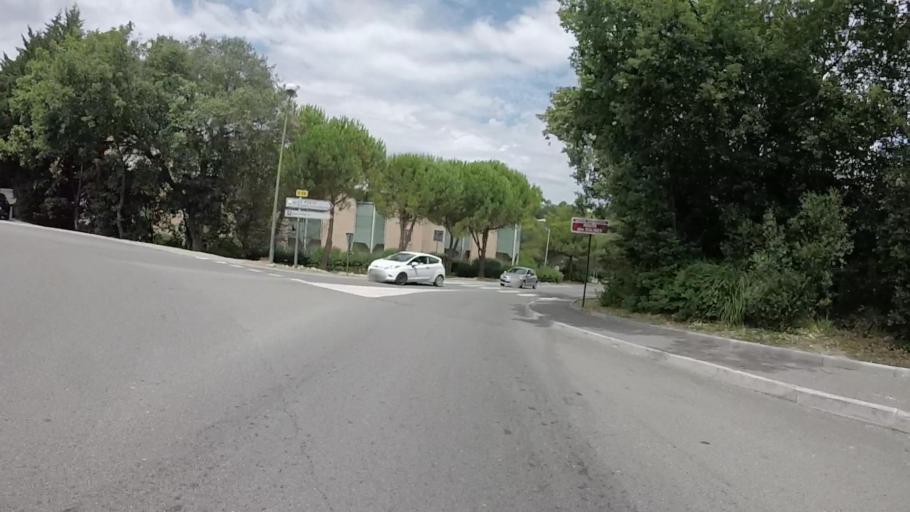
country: FR
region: Provence-Alpes-Cote d'Azur
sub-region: Departement des Alpes-Maritimes
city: Vallauris
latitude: 43.6240
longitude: 7.0497
